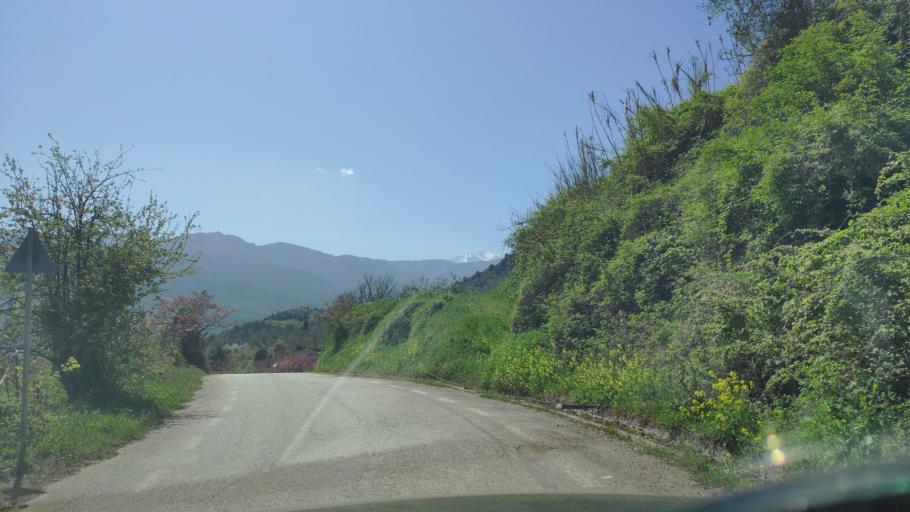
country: GR
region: West Greece
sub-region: Nomos Achaias
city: Akrata
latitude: 38.1022
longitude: 22.3175
